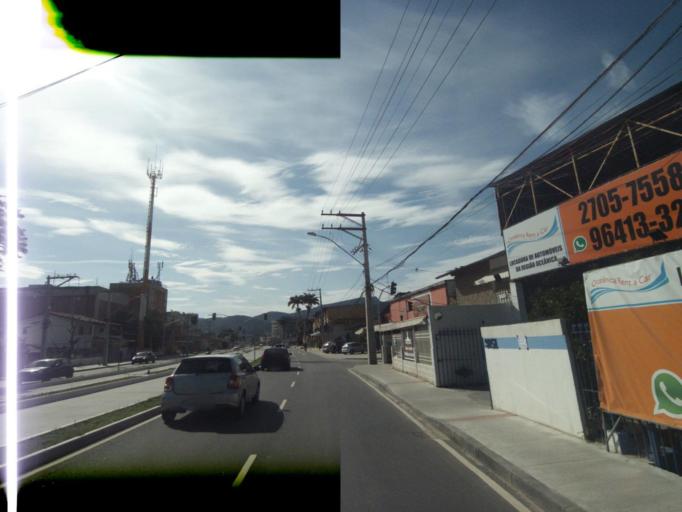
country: BR
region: Rio de Janeiro
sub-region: Niteroi
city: Niteroi
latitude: -22.9487
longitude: -43.0301
